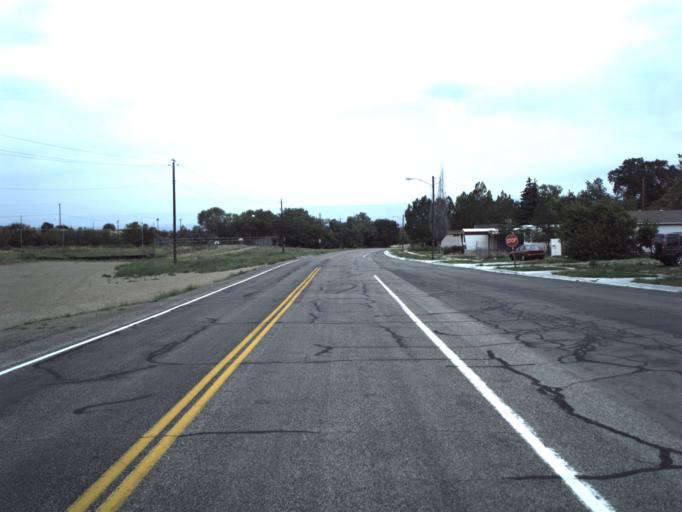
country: US
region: Utah
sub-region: Carbon County
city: East Carbon City
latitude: 39.5504
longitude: -110.3882
